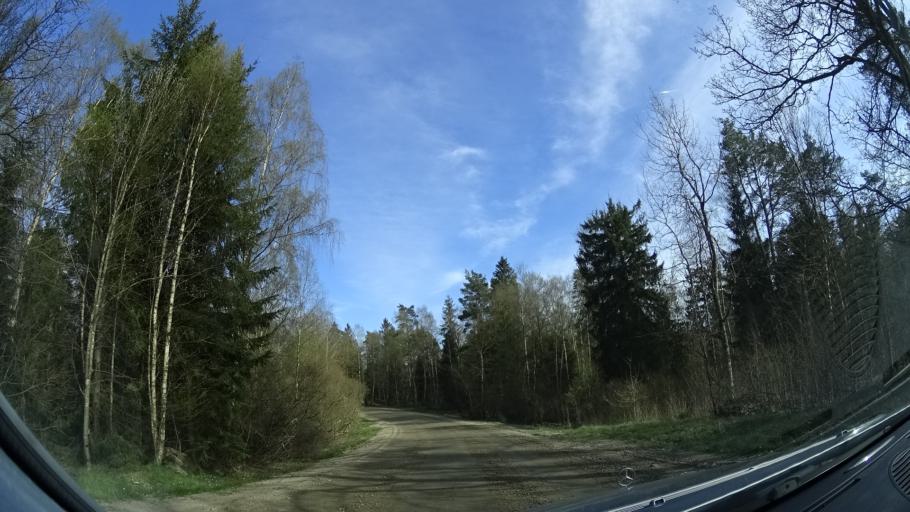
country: SE
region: Skane
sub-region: Hassleholms Kommun
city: Sosdala
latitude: 56.0870
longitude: 13.6828
